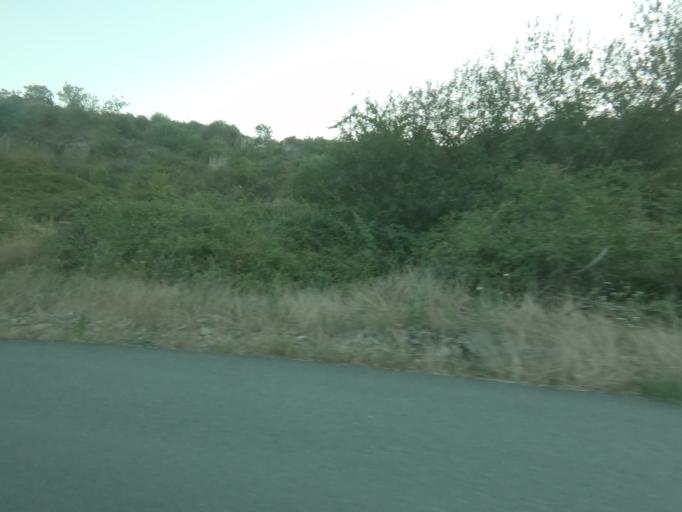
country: PT
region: Vila Real
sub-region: Peso da Regua
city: Peso da Regua
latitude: 41.1481
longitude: -7.7329
